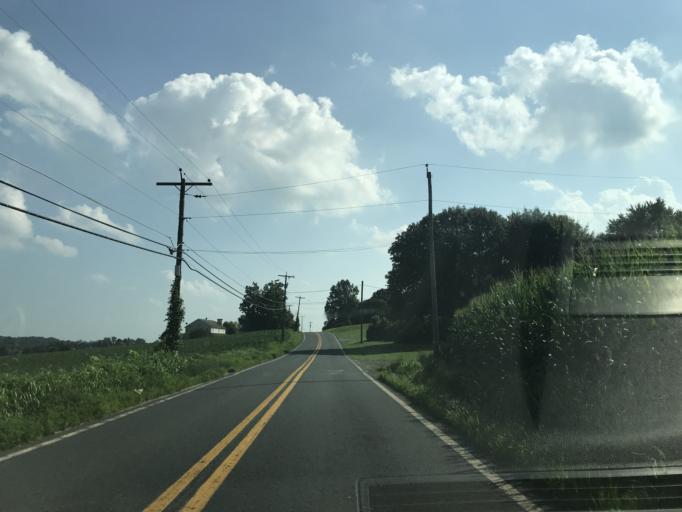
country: US
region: Maryland
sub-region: Carroll County
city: Westminster
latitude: 39.6148
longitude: -76.9813
